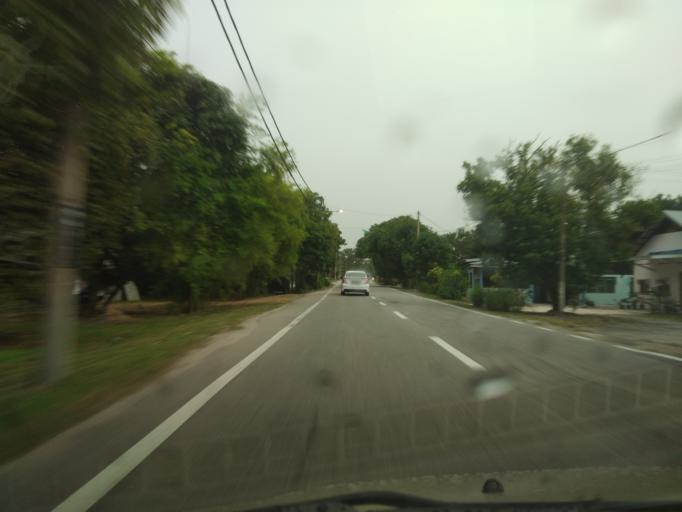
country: MY
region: Penang
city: Permatang Kuching
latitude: 5.4838
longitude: 100.4009
